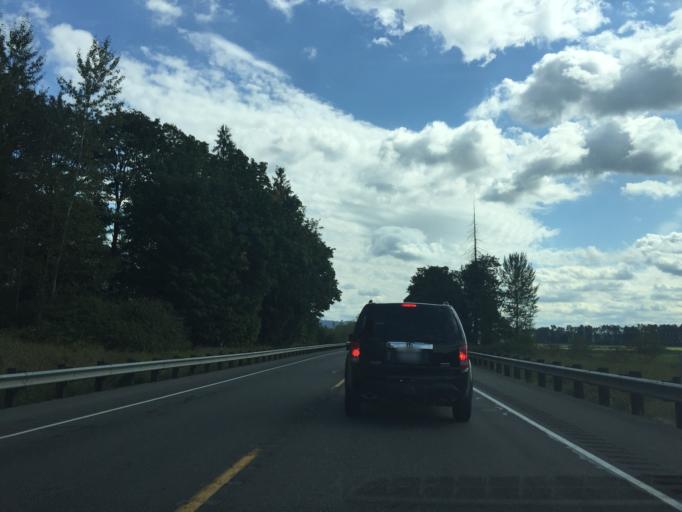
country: US
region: Washington
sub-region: Snohomish County
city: Three Lakes
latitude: 47.8929
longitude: -122.0301
